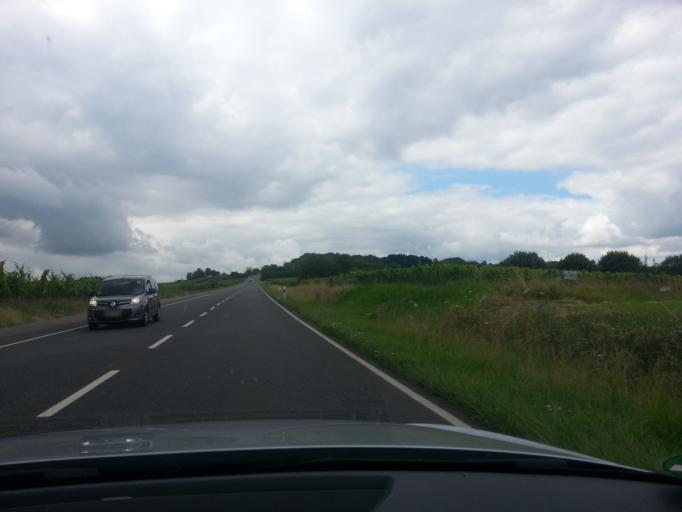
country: LU
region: Grevenmacher
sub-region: Canton de Remich
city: Remich
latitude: 49.5395
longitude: 6.3513
